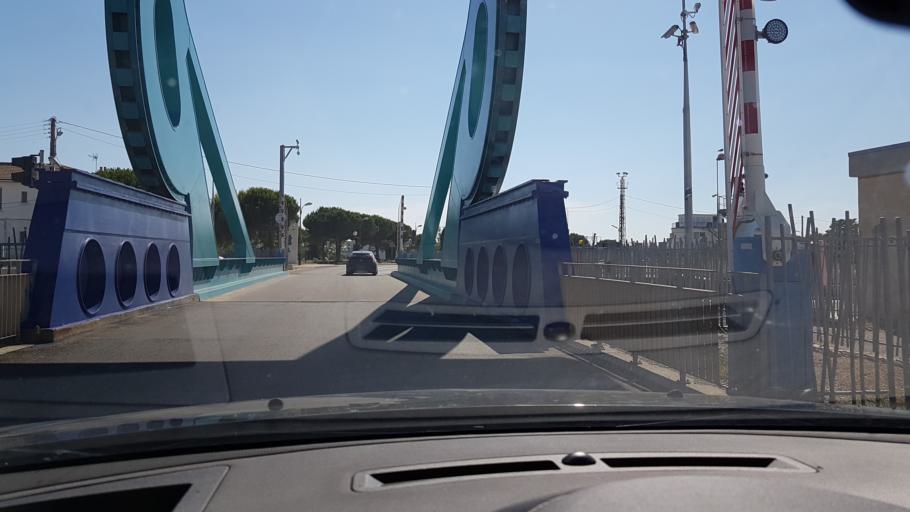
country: FR
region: Provence-Alpes-Cote d'Azur
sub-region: Departement des Bouches-du-Rhone
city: Port-Saint-Louis-du-Rhone
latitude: 43.3839
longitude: 4.8085
